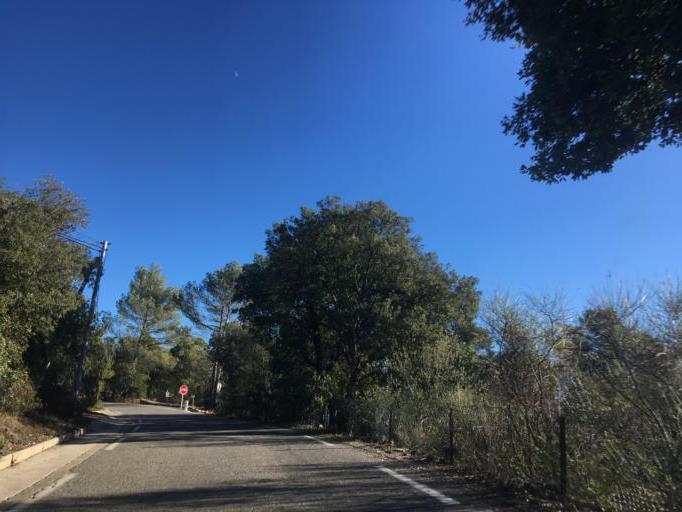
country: FR
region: Provence-Alpes-Cote d'Azur
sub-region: Departement du Var
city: Barjols
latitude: 43.5930
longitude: 6.0342
